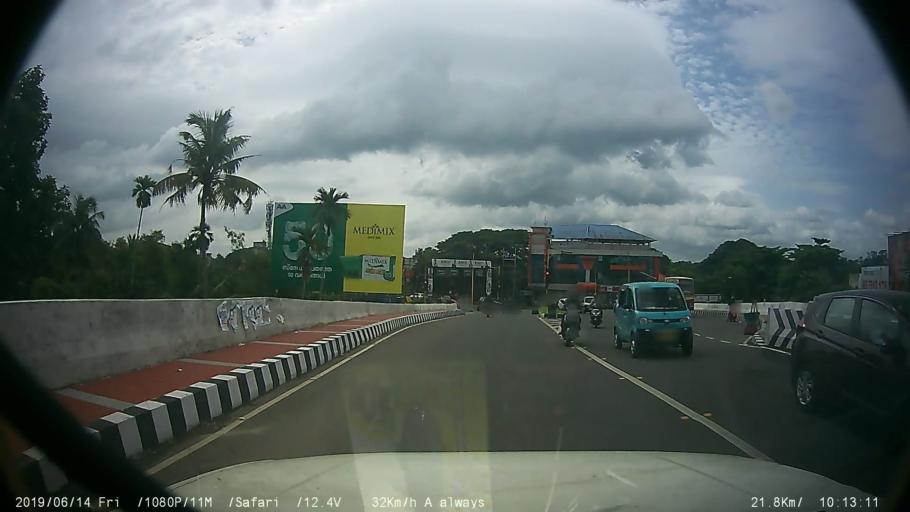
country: IN
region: Kerala
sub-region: Kottayam
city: Kottayam
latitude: 9.5976
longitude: 76.5269
